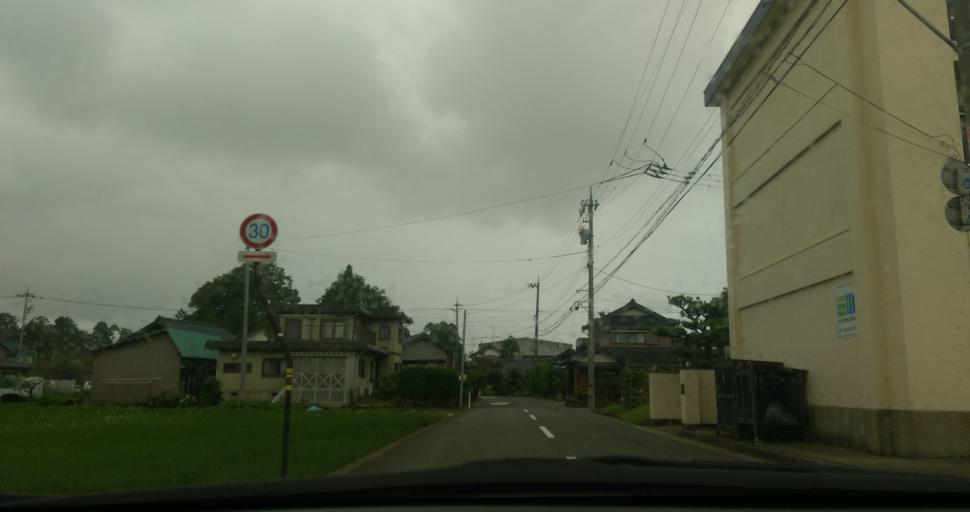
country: JP
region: Fukui
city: Fukui-shi
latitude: 36.0242
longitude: 136.2329
